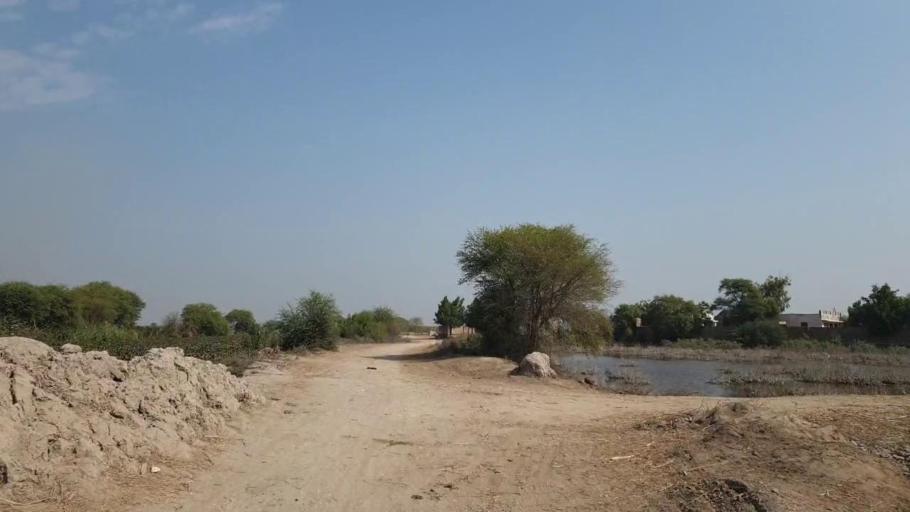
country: PK
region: Sindh
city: Tando Muhammad Khan
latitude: 25.0784
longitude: 68.4217
